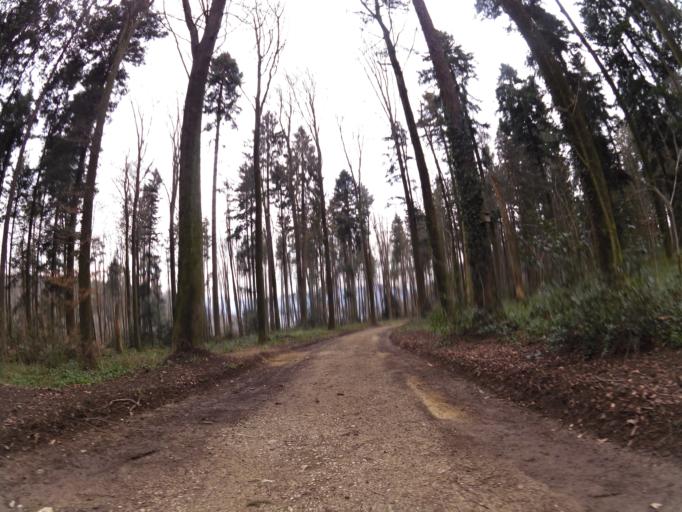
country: CH
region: Aargau
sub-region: Bezirk Aarau
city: Aarau
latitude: 47.3779
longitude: 8.0324
